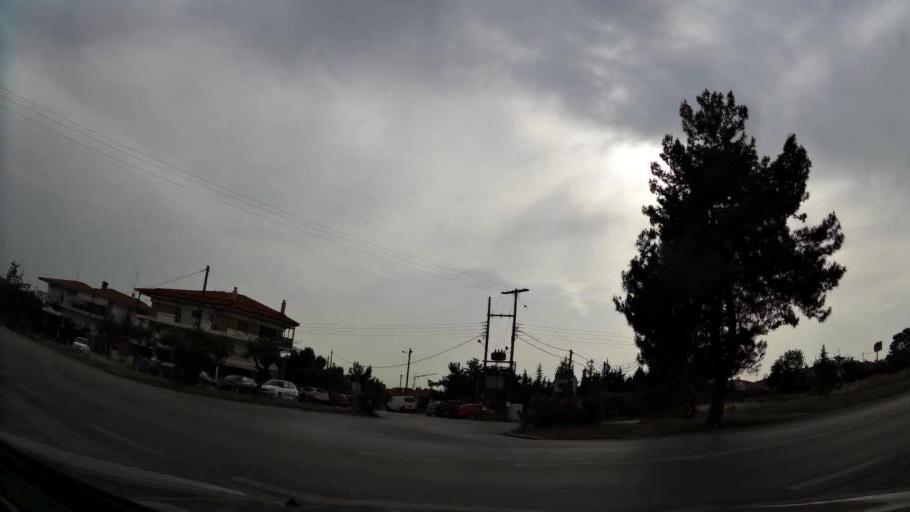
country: GR
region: Central Macedonia
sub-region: Nomos Thessalonikis
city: Oraiokastro
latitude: 40.7106
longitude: 22.9298
